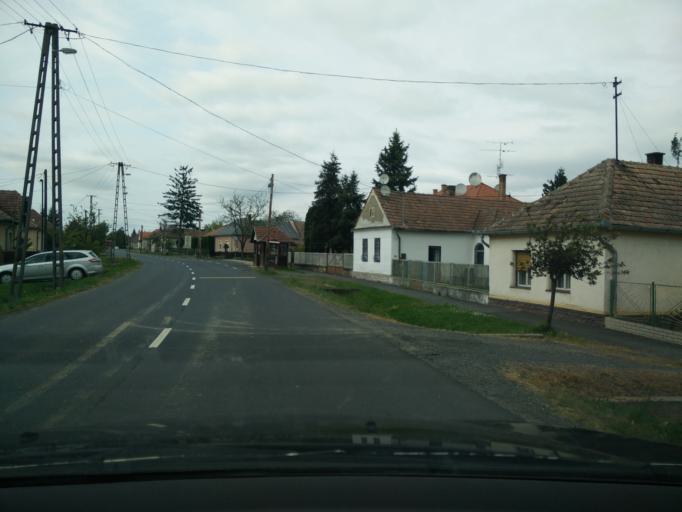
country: HU
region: Zala
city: Zalaszentgrot
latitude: 46.9879
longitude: 17.0363
